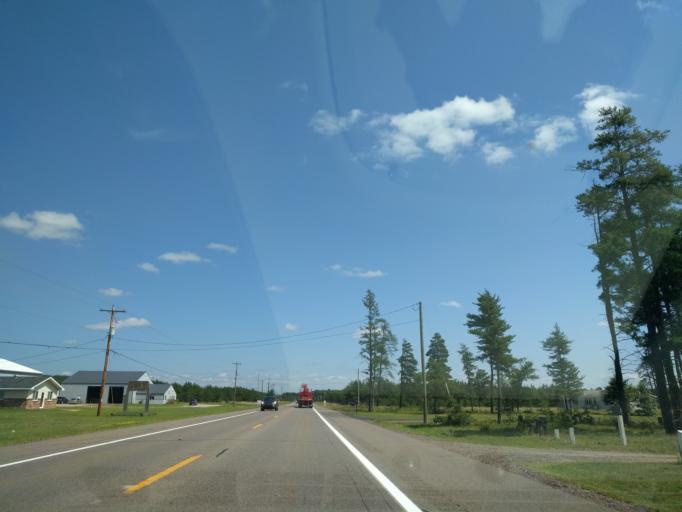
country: US
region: Michigan
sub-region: Marquette County
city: K. I. Sawyer Air Force Base
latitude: 46.2838
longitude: -87.3716
